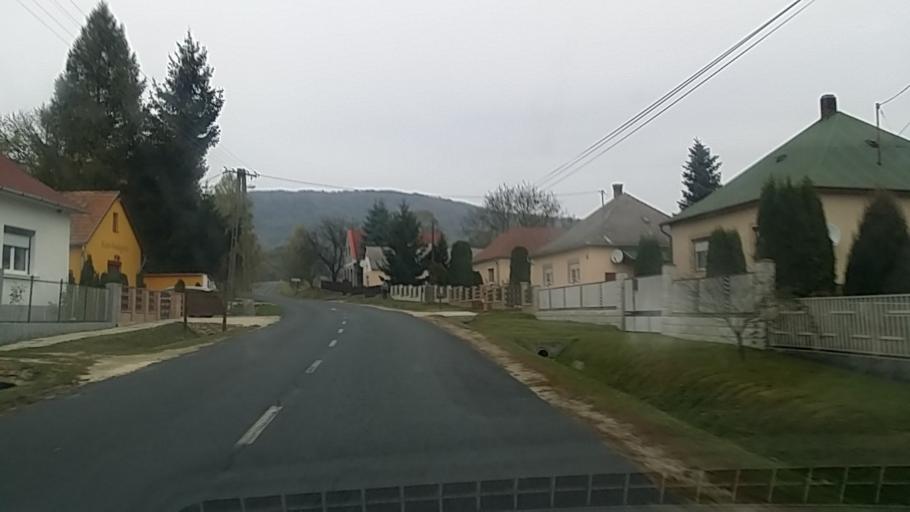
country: HU
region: Veszprem
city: Zirc
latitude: 47.2353
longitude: 17.7844
